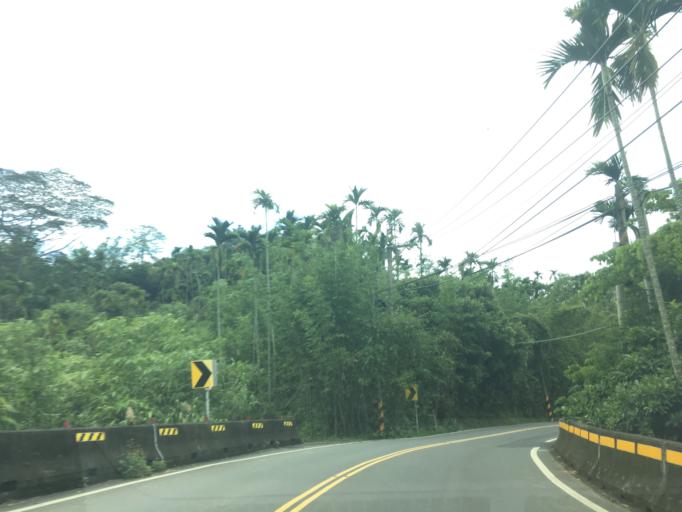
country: TW
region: Taiwan
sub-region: Yunlin
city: Douliu
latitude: 23.5704
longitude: 120.5675
